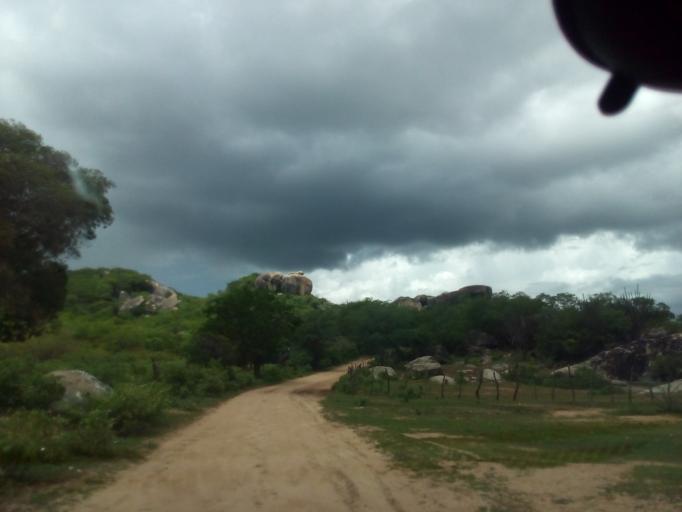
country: BR
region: Rio Grande do Norte
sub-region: Sao Tome
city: Sao Tome
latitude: -5.9508
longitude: -35.9233
